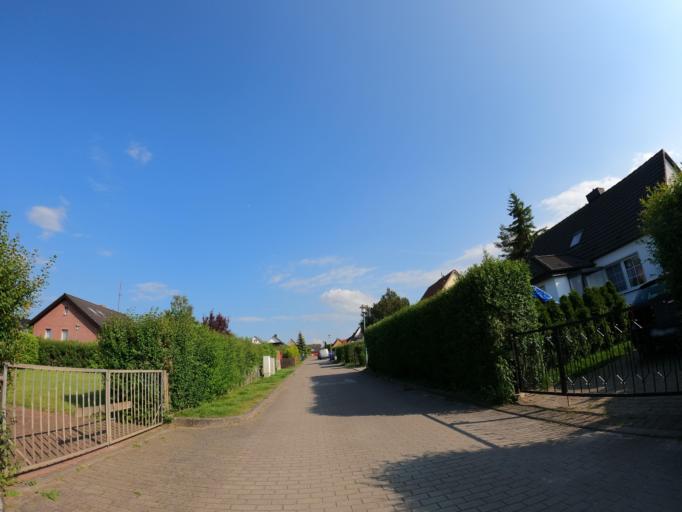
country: DE
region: Mecklenburg-Vorpommern
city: Stralsund
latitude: 54.2968
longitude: 13.0621
